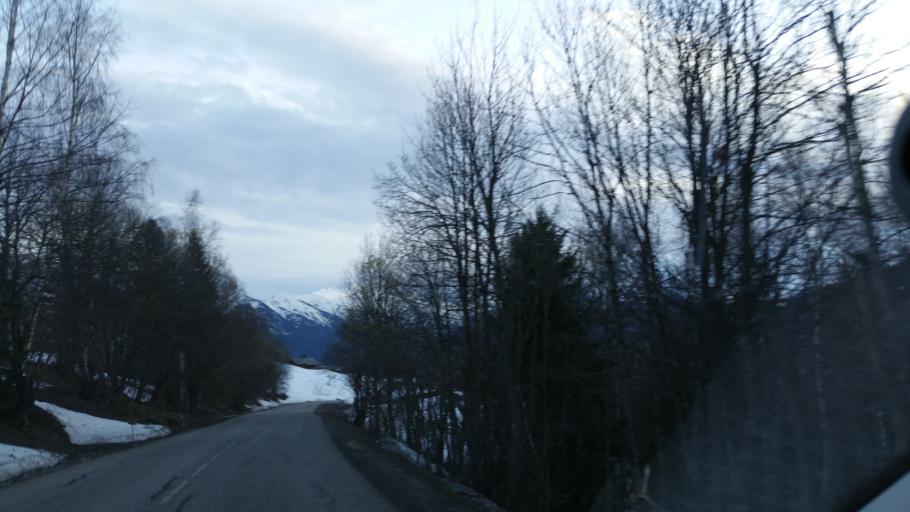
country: FR
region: Rhone-Alpes
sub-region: Departement de la Savoie
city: La Chambre
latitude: 45.4122
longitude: 6.3488
